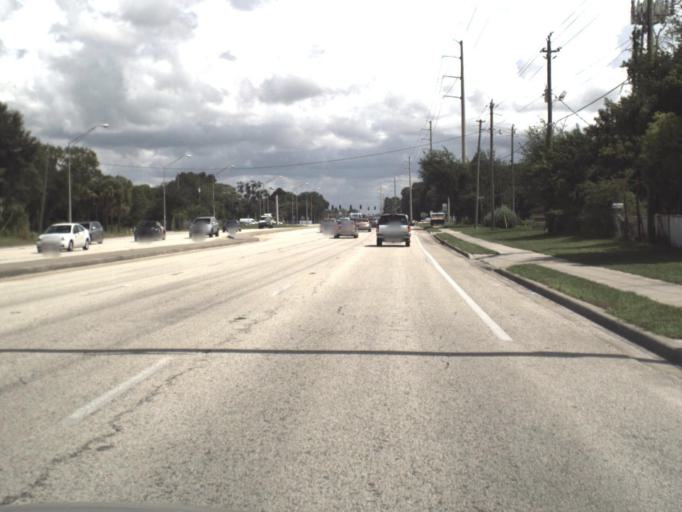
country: US
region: Florida
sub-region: Manatee County
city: Samoset
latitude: 27.4474
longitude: -82.5341
